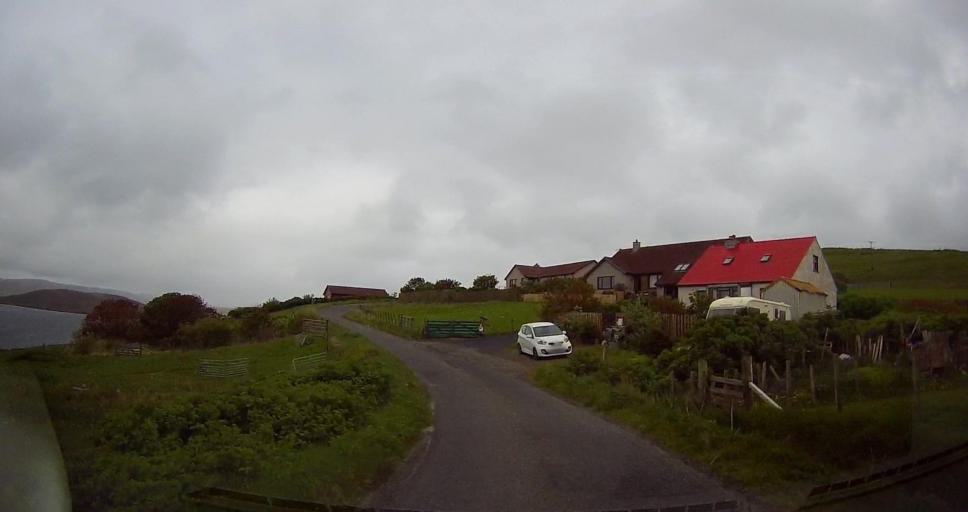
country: GB
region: Scotland
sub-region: Shetland Islands
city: Lerwick
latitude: 60.3729
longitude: -1.3827
